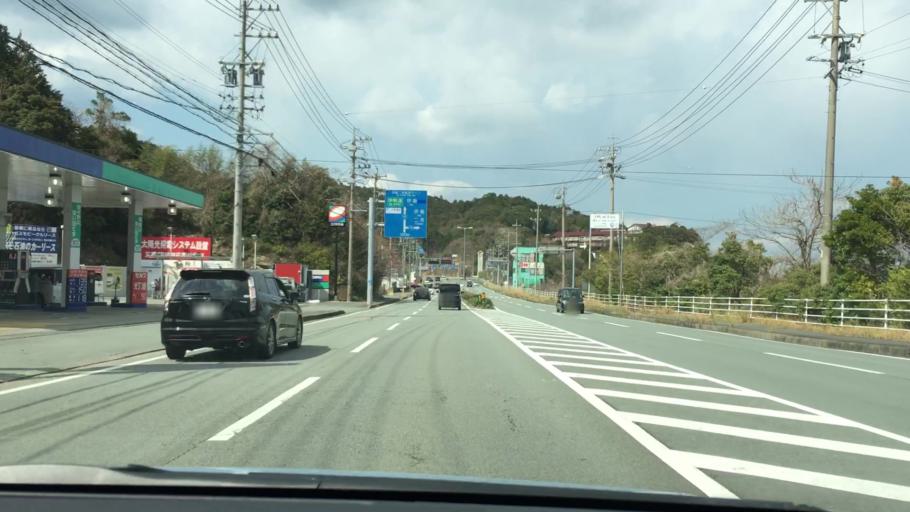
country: JP
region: Mie
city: Toba
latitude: 34.4827
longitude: 136.8161
